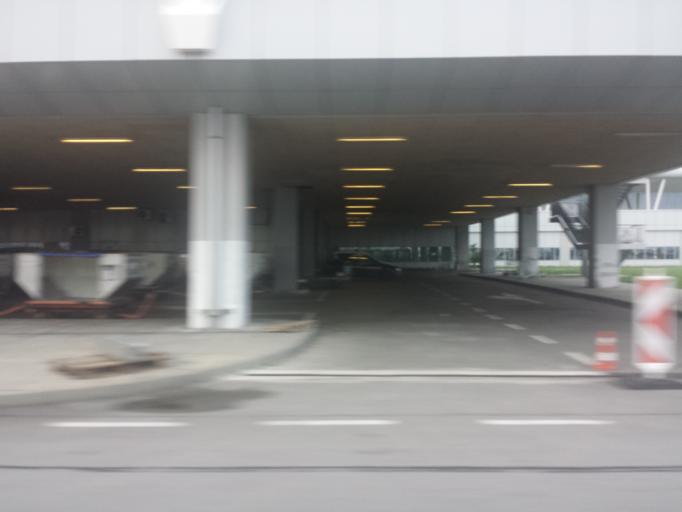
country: BG
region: Sofia-Capital
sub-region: Stolichna Obshtina
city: Sofia
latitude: 42.6893
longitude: 23.4134
